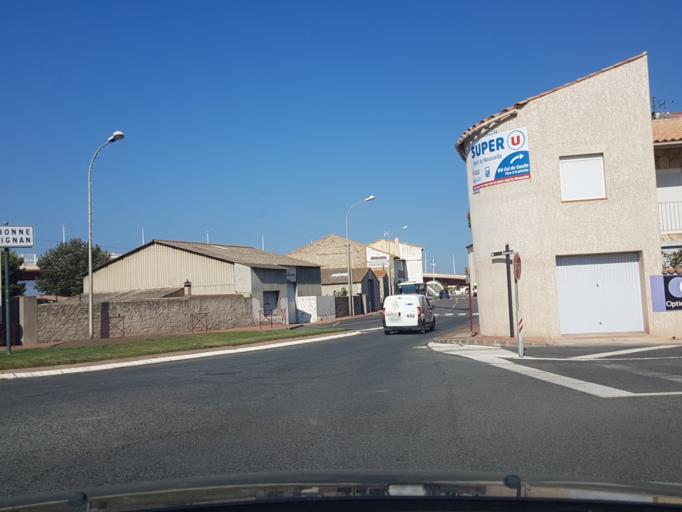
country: FR
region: Languedoc-Roussillon
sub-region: Departement de l'Aude
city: Port-la-Nouvelle
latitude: 43.0225
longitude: 3.0395
